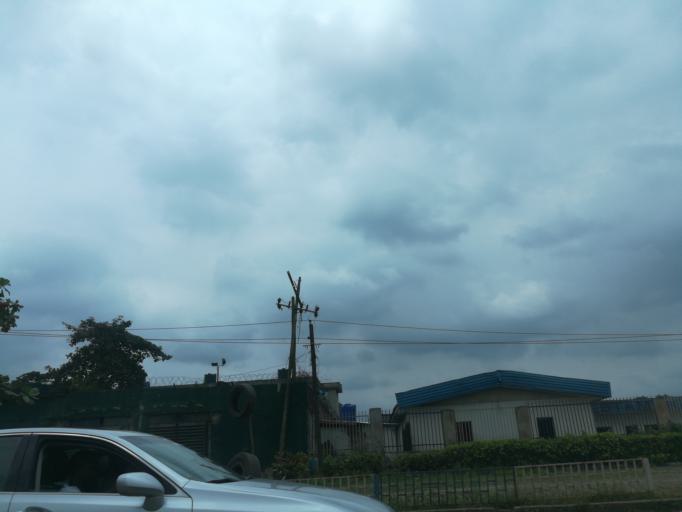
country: NG
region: Lagos
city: Ikeja
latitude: 6.6040
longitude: 3.3323
